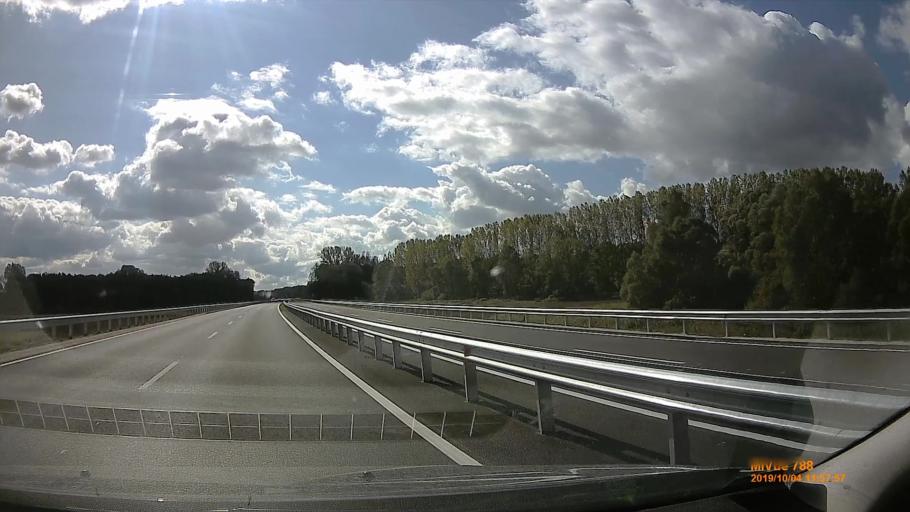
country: HU
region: Somogy
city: Karad
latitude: 46.6546
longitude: 17.7866
